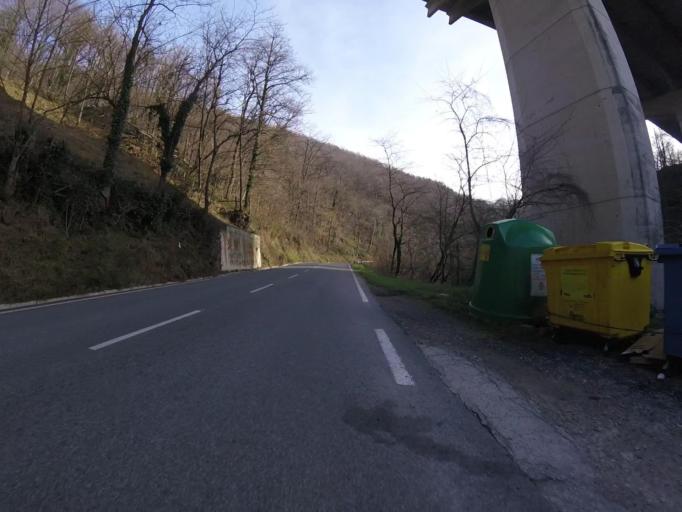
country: ES
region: Navarre
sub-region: Provincia de Navarra
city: Areso
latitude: 43.0955
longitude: -1.9427
